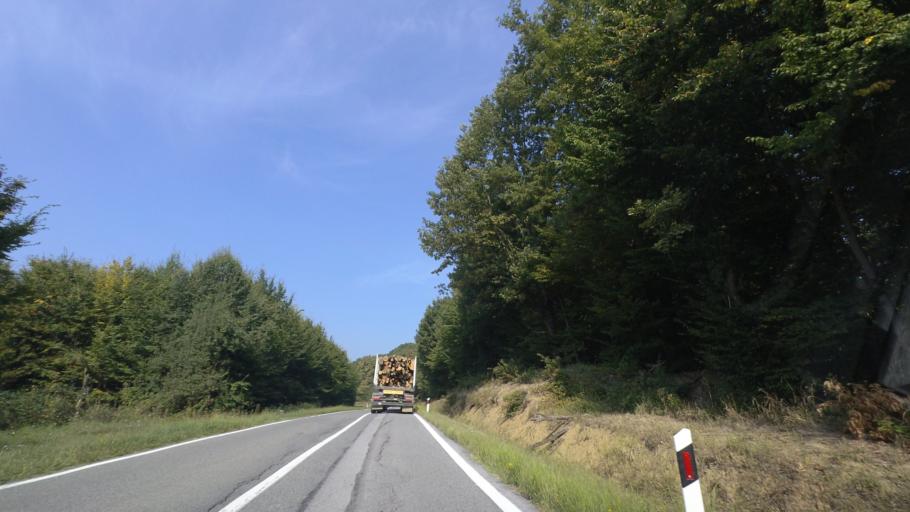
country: HR
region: Pozesko-Slavonska
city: Lipik
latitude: 45.4193
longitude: 17.0921
